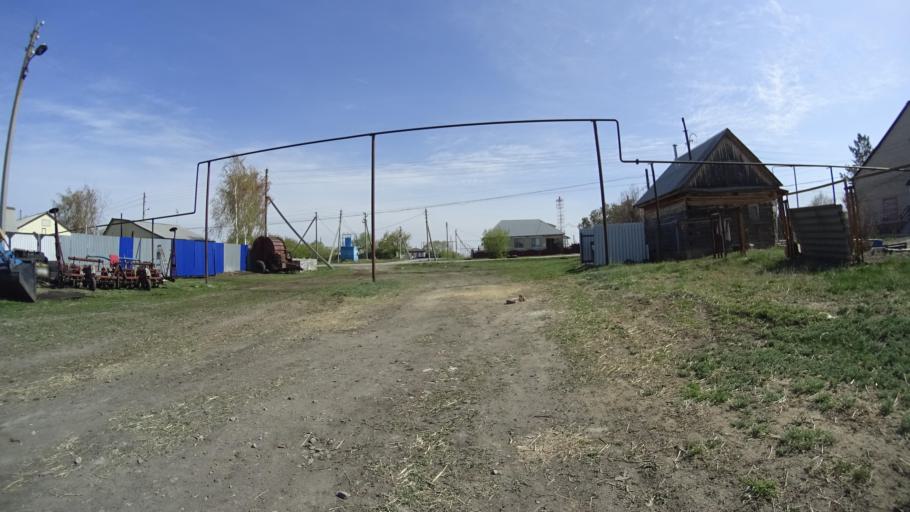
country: RU
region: Chelyabinsk
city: Chesma
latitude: 53.7914
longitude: 61.0359
